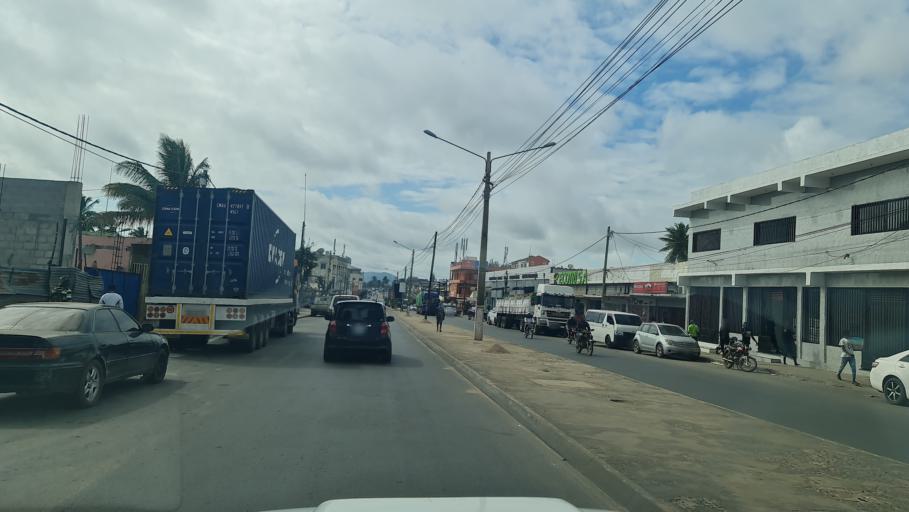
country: MZ
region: Nampula
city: Nampula
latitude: -15.1145
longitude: 39.2759
